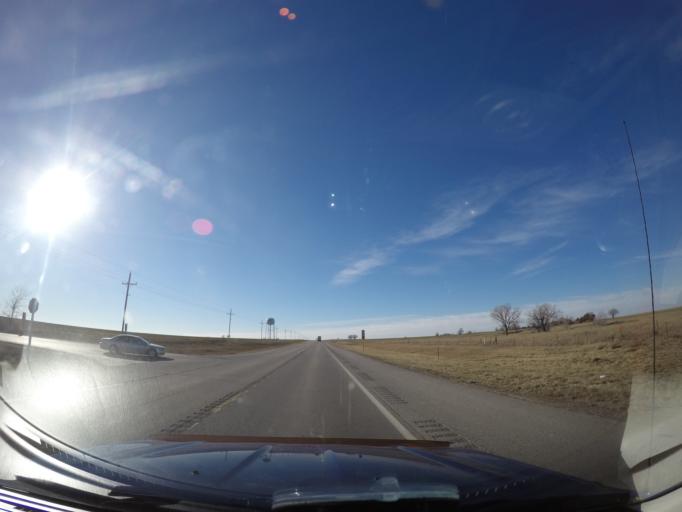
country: US
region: Kansas
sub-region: Marion County
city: Hillsboro
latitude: 38.3627
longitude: -97.2463
